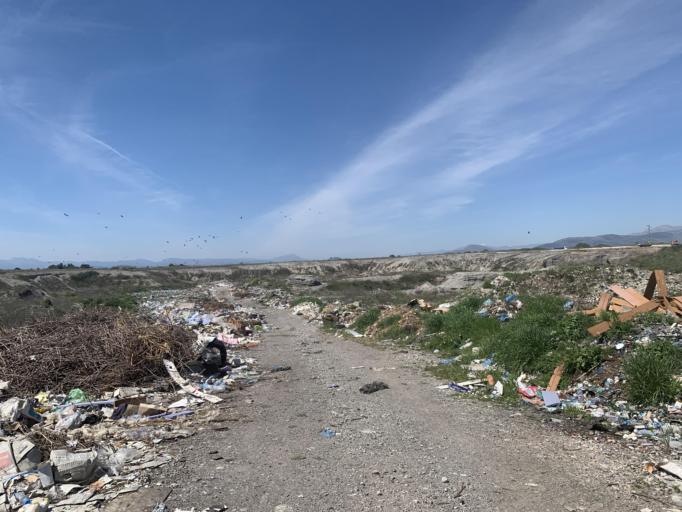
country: AL
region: Shkoder
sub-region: Rrethi i Malesia e Madhe
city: Koplik
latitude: 42.2299
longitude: 19.4336
